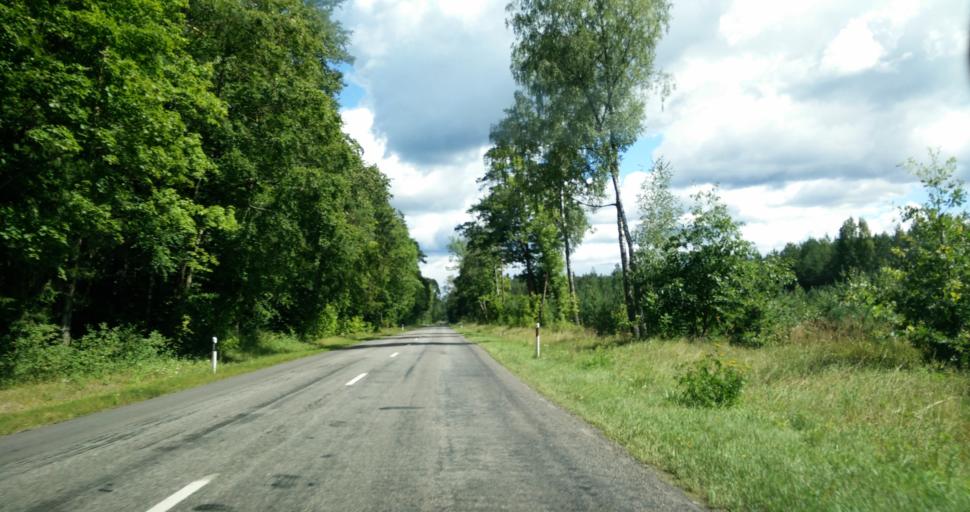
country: LT
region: Taurages apskritis
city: Taurage
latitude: 55.0987
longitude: 22.2280
